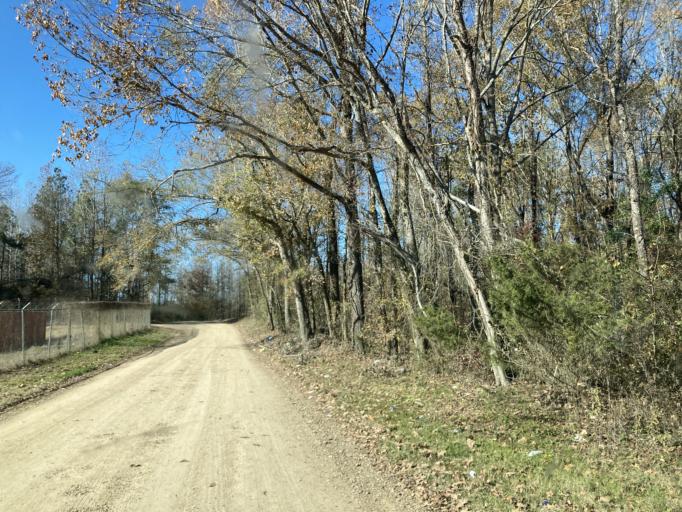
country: US
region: Mississippi
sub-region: Holmes County
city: Pickens
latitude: 32.8561
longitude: -90.0147
